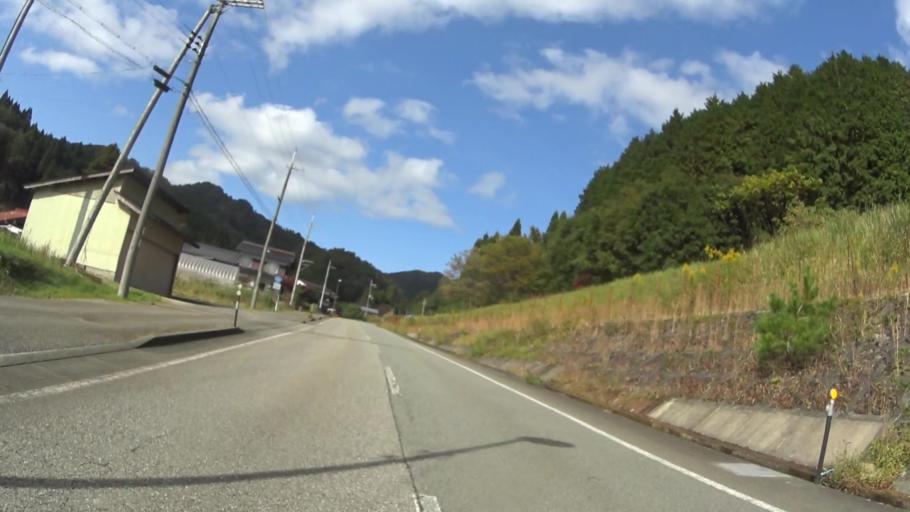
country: JP
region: Hyogo
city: Toyooka
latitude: 35.5107
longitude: 134.9923
